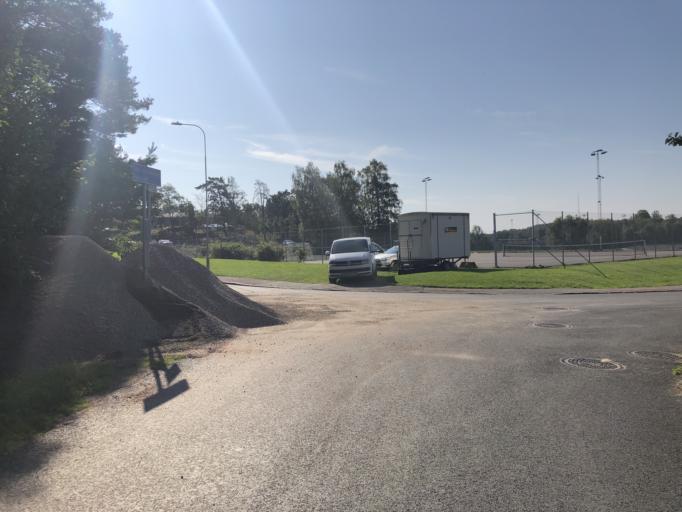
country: SE
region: Vaestra Goetaland
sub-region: Goteborg
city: Goeteborg
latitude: 57.7476
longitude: 11.9657
